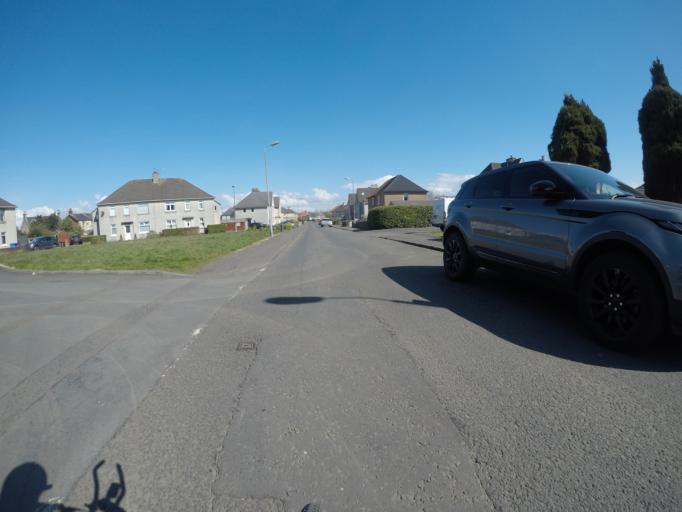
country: GB
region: Scotland
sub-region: North Ayrshire
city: Irvine
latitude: 55.6169
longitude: -4.6563
